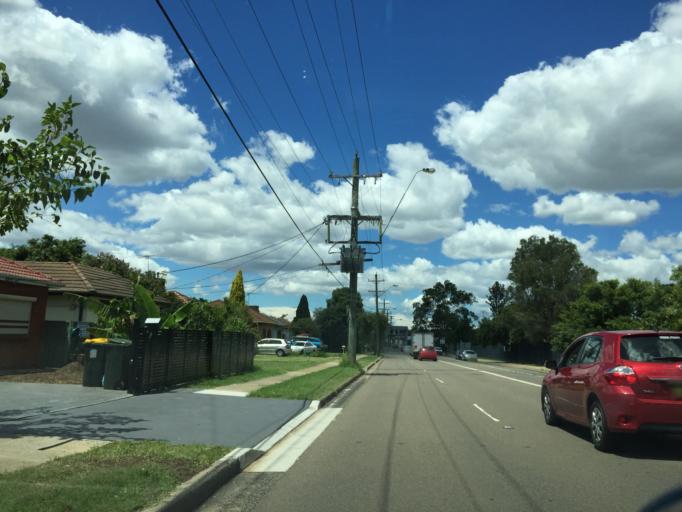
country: AU
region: New South Wales
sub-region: Blacktown
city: Blacktown
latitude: -33.7693
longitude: 150.9380
